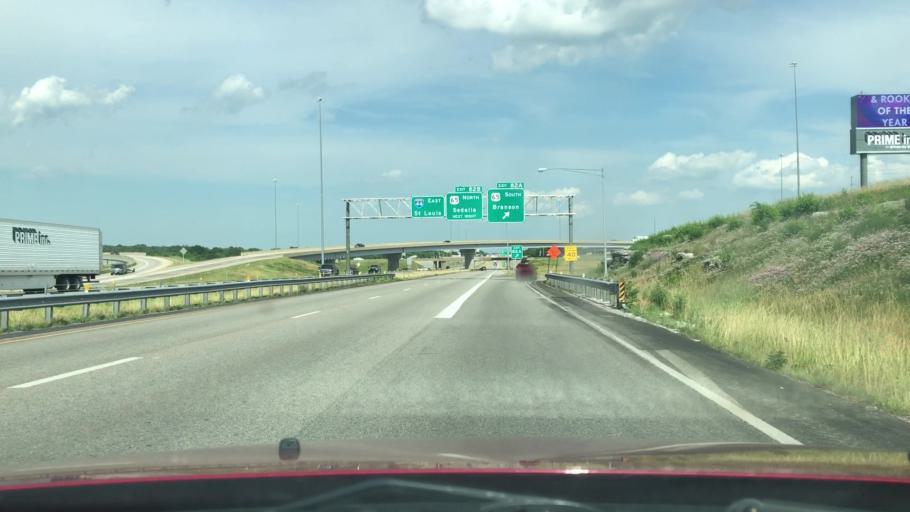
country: US
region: Missouri
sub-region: Greene County
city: Springfield
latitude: 37.2501
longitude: -93.2297
